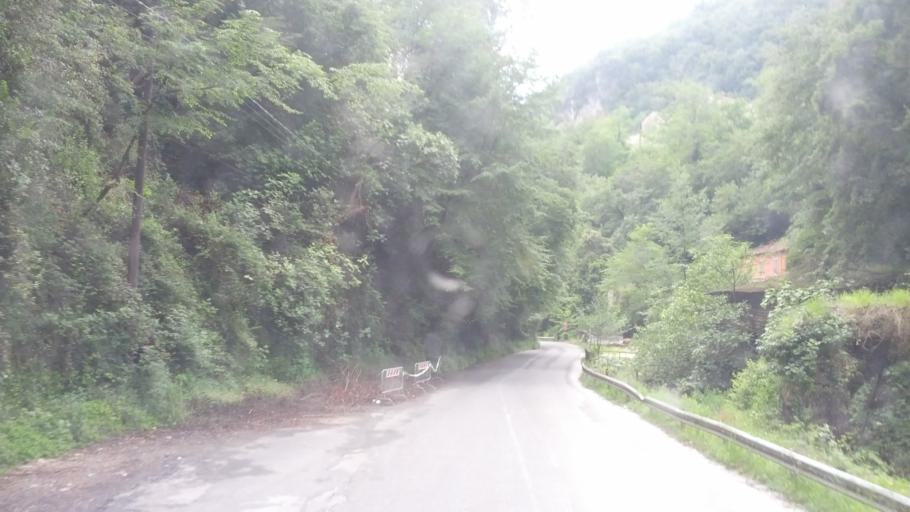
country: IT
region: Tuscany
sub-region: Provincia di Massa-Carrara
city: Carrara
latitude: 44.0874
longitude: 10.1038
